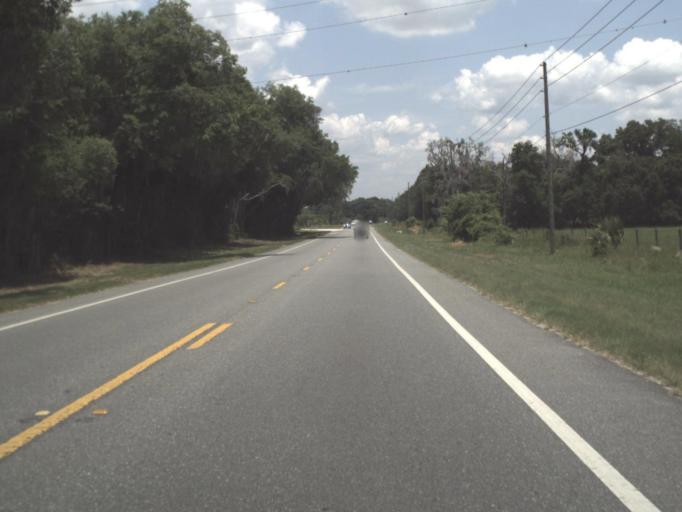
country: US
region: Florida
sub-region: Alachua County
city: Newberry
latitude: 29.6447
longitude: -82.6500
